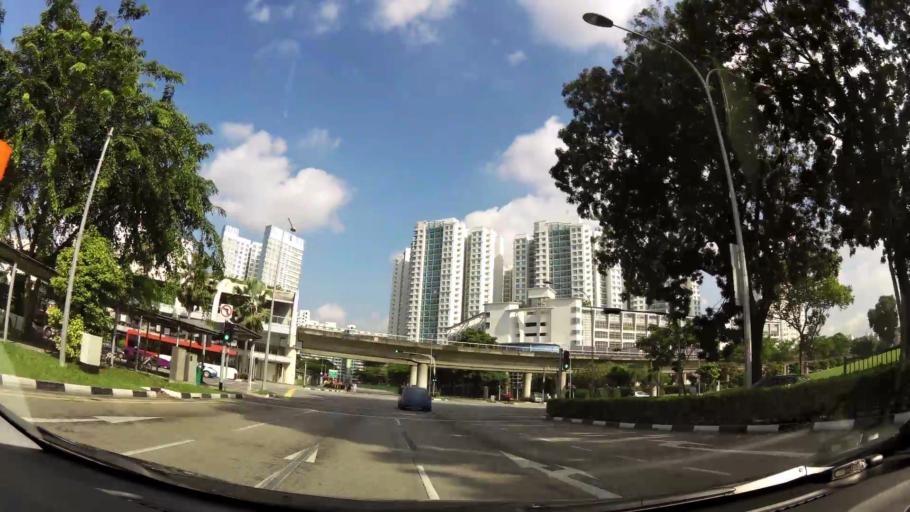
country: SG
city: Singapore
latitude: 1.3112
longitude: 103.8722
